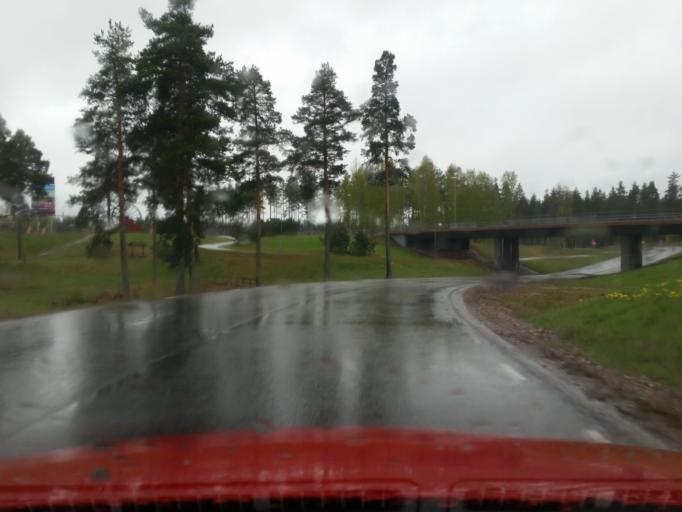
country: SE
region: Dalarna
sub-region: Leksand Municipality
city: Smedby
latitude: 60.6761
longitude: 15.0873
